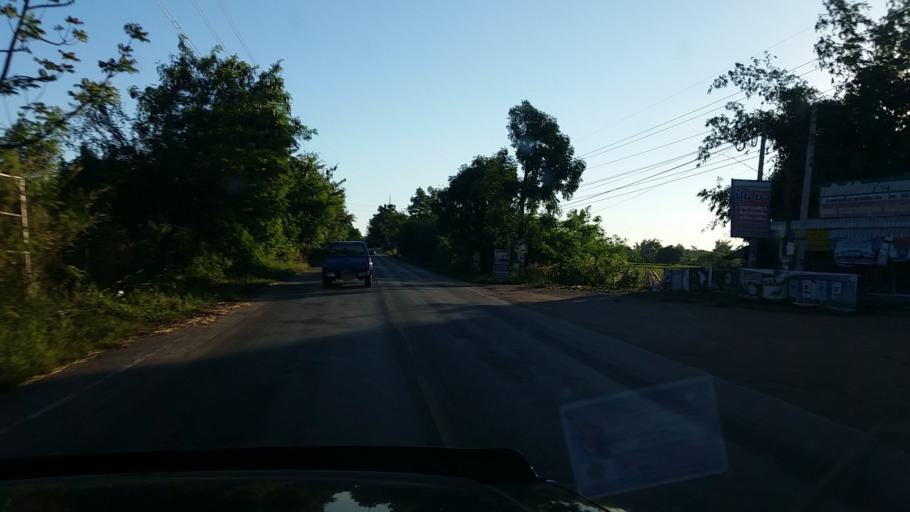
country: TH
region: Chaiyaphum
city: Nong Bua Rawe
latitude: 15.7197
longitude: 101.7422
